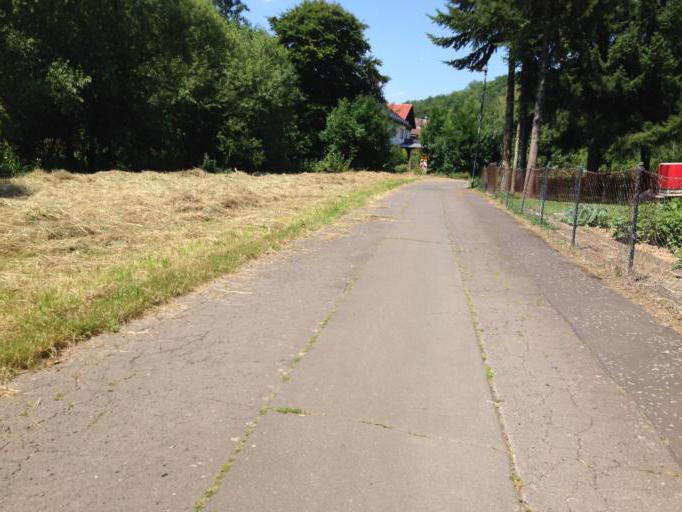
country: DE
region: Hesse
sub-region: Regierungsbezirk Giessen
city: Heuchelheim
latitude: 50.6169
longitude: 8.6443
